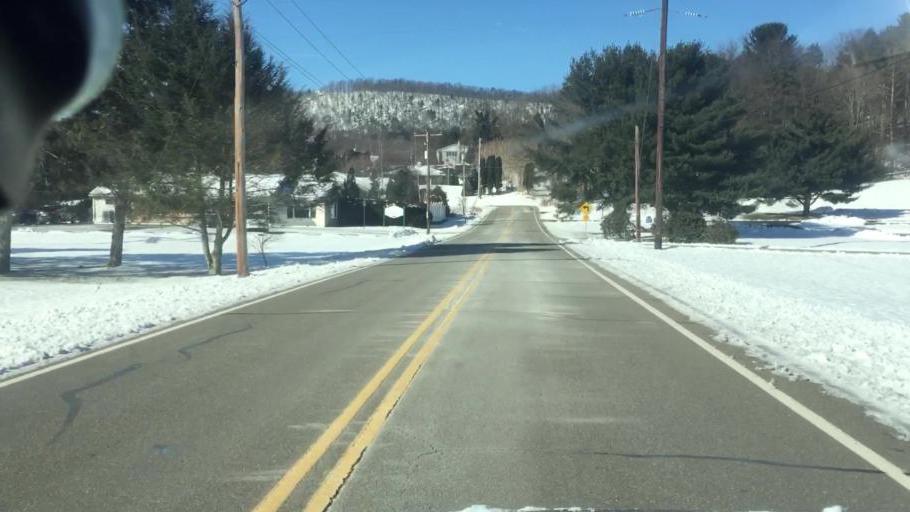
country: US
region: Pennsylvania
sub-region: Luzerne County
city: East Berwick
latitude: 41.0709
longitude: -76.2345
